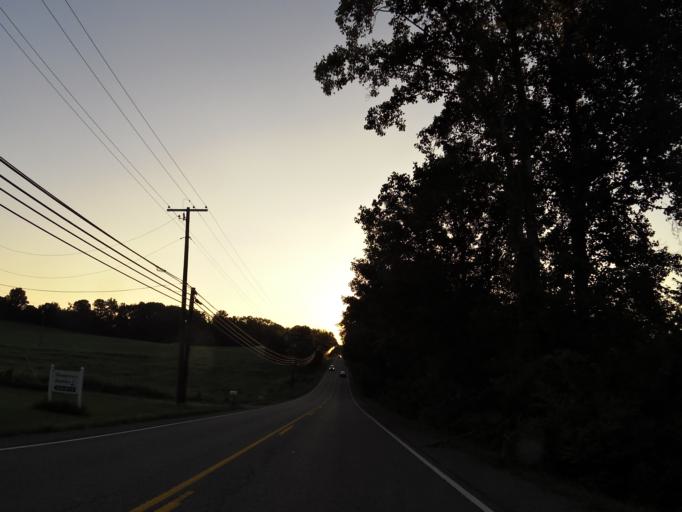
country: US
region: Tennessee
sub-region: Knox County
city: Mascot
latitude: 36.0188
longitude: -83.6903
